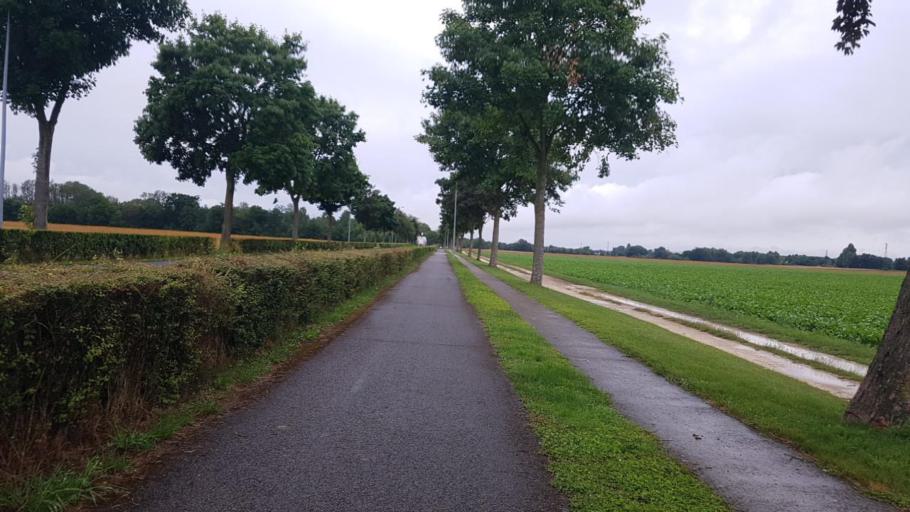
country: FR
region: Champagne-Ardenne
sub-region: Departement de la Marne
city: Sarry
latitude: 48.9253
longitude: 4.3977
